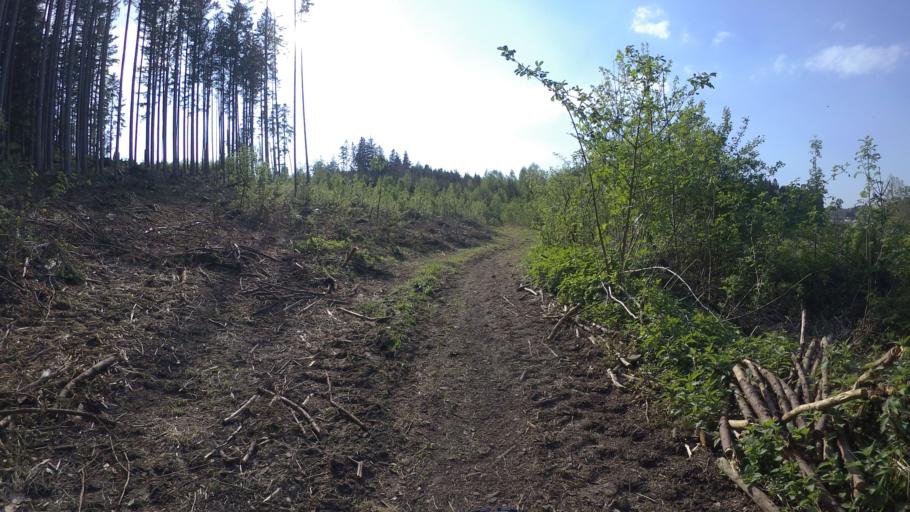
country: DE
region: Bavaria
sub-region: Upper Bavaria
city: Chieming
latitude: 47.9079
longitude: 12.5504
